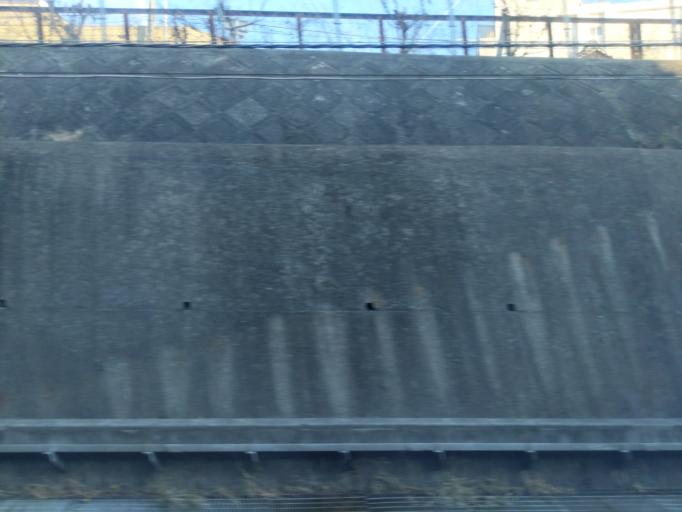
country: JP
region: Aichi
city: Nagoya-shi
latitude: 35.1798
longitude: 136.9372
